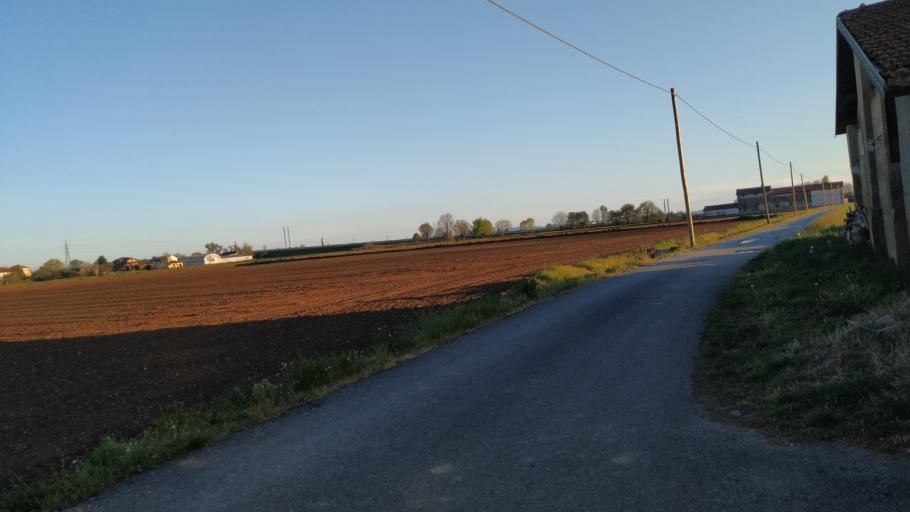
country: IT
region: Piedmont
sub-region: Provincia di Vercelli
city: Santhia
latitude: 45.3612
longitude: 8.1677
